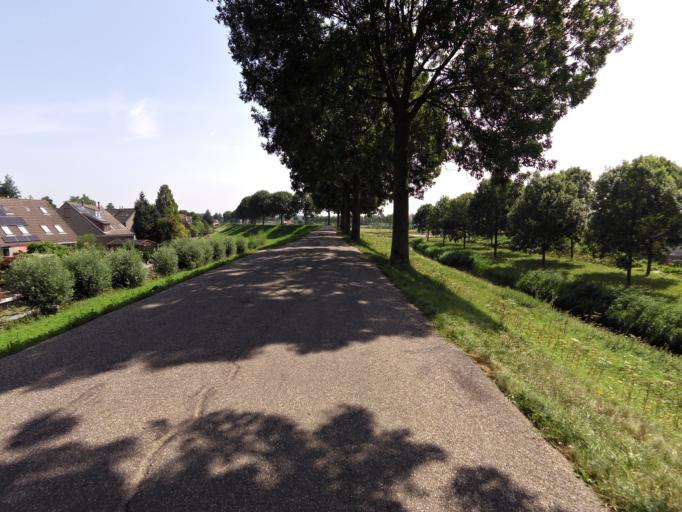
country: NL
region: South Holland
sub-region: Gemeente Papendrecht
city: Papendrecht
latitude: 51.7976
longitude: 4.7188
